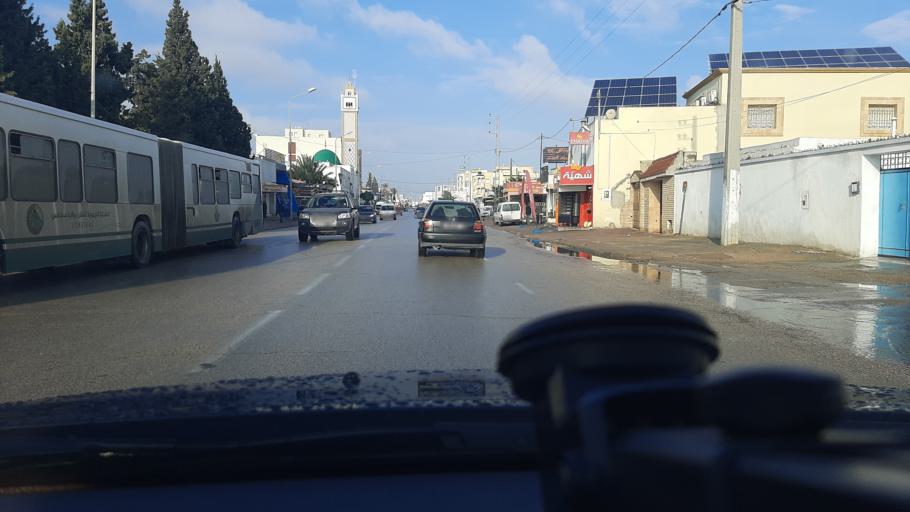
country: TN
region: Safaqis
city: Sfax
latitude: 34.7444
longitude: 10.7297
